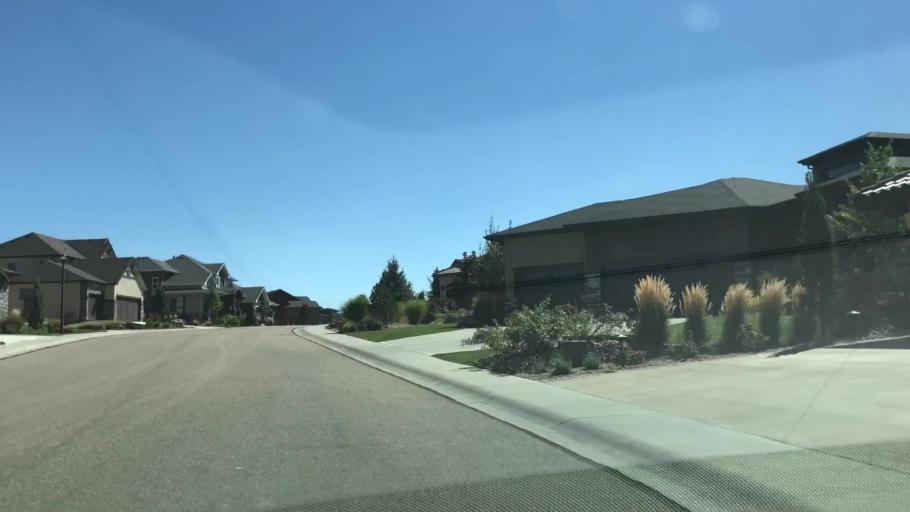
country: US
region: Colorado
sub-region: Weld County
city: Windsor
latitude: 40.4535
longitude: -104.9624
